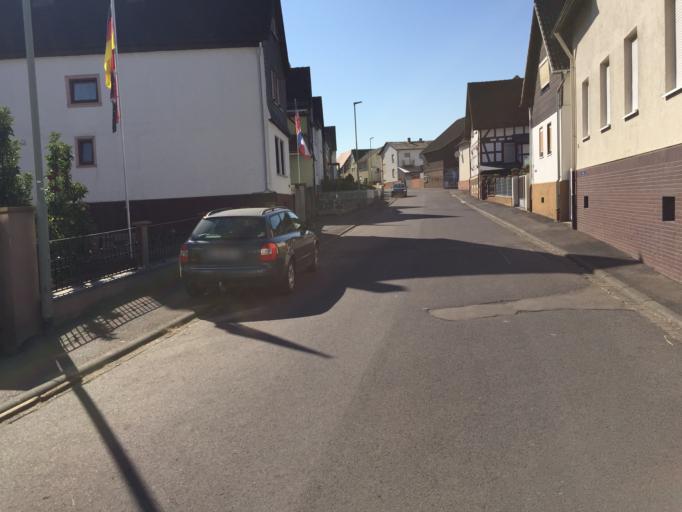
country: DE
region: Hesse
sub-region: Regierungsbezirk Darmstadt
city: Nidda
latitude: 50.4336
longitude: 8.9752
